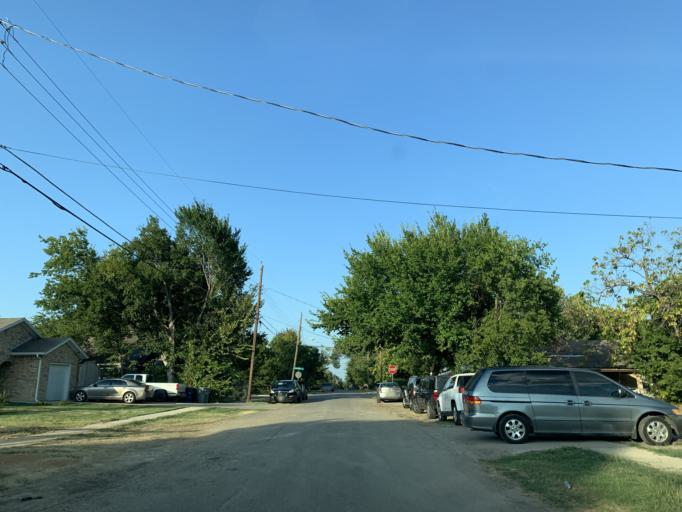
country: US
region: Texas
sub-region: Dallas County
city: Dallas
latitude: 32.7021
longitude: -96.7872
